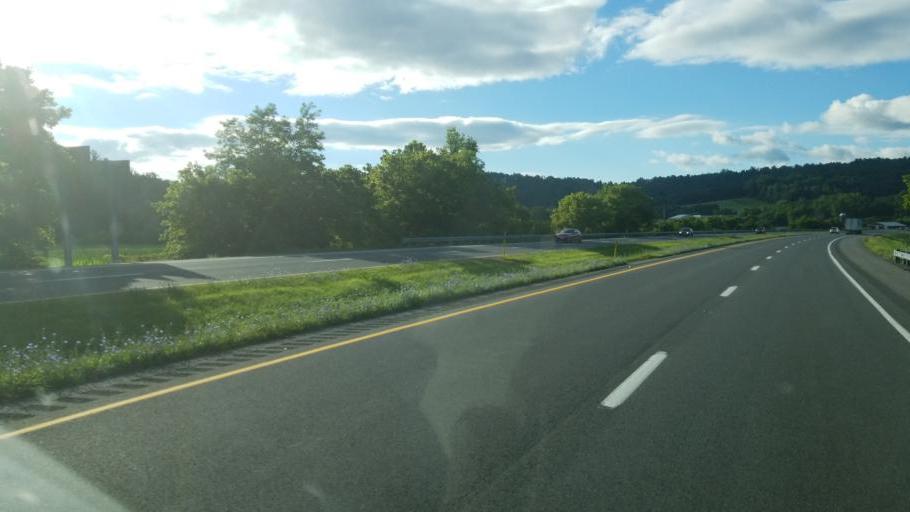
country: US
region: Maryland
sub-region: Washington County
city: Hancock
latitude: 39.7536
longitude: -78.1850
